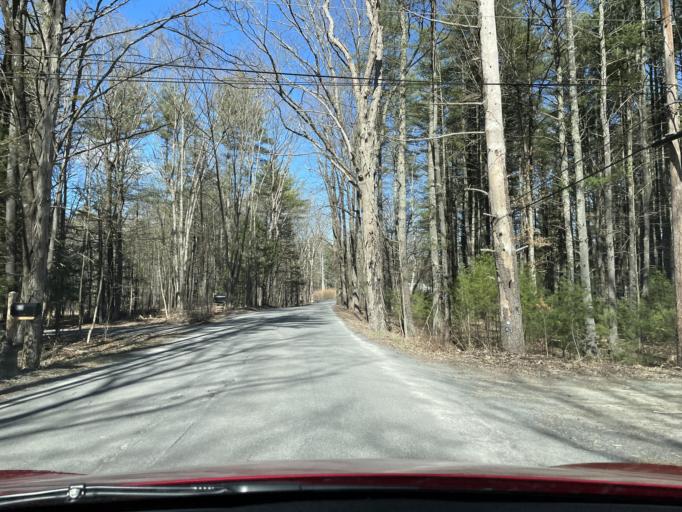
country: US
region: New York
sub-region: Ulster County
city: Zena
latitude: 42.0428
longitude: -74.0621
